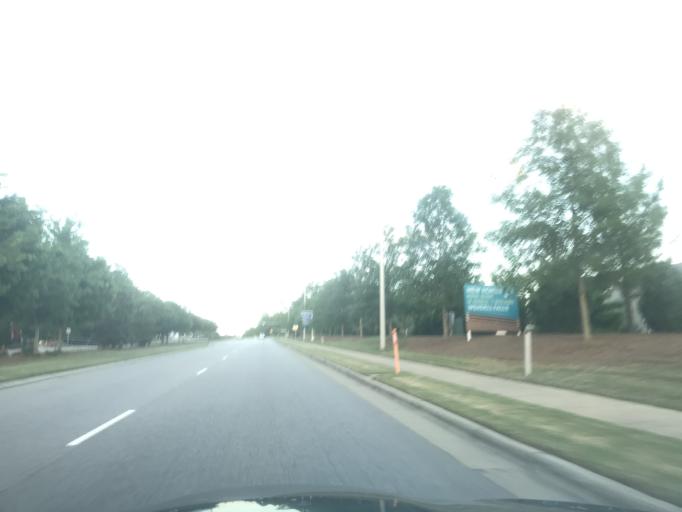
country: US
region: North Carolina
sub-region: Wake County
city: Wendell
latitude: 35.7693
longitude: -78.4210
